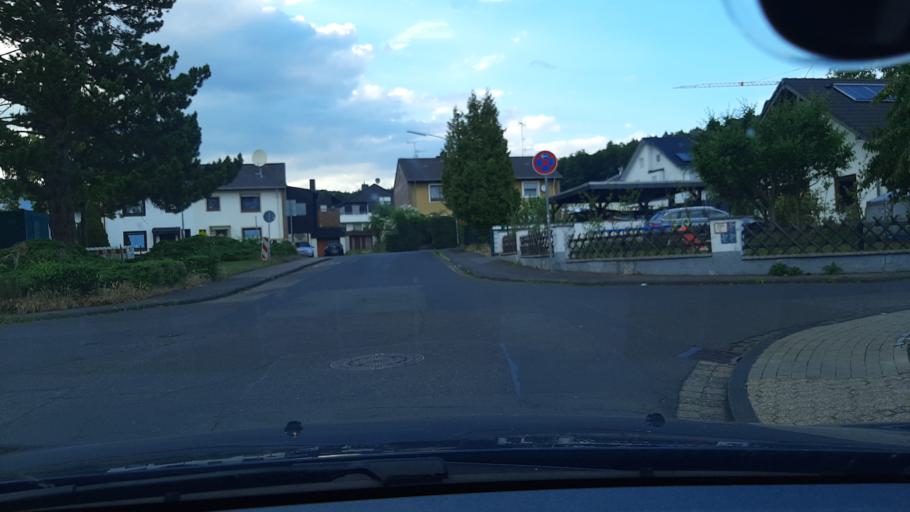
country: DE
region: North Rhine-Westphalia
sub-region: Regierungsbezirk Koln
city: Mechernich
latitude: 50.5937
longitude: 6.6492
